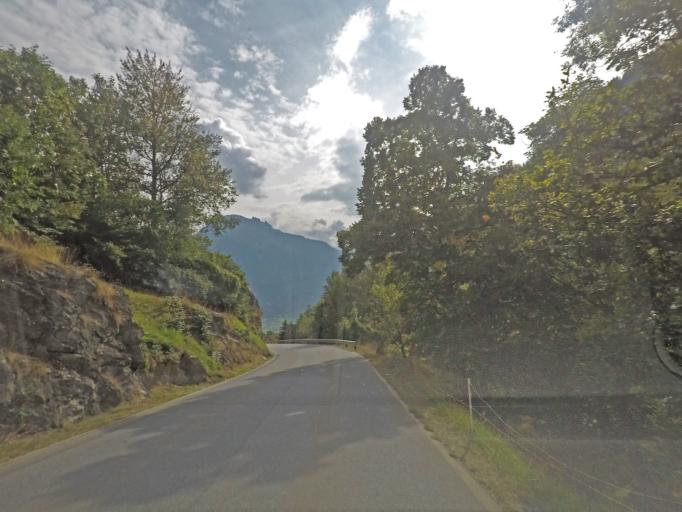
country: CH
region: Valais
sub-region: Brig District
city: Naters
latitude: 46.3387
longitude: 7.9835
